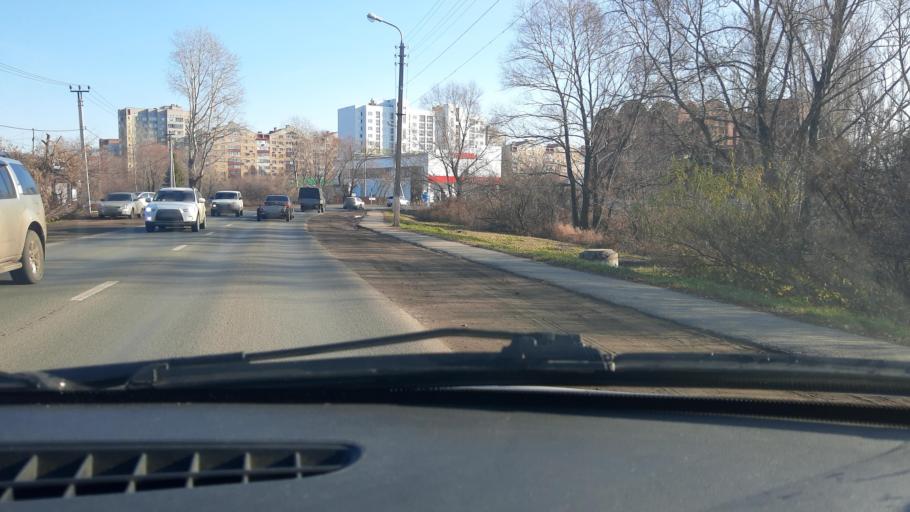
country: RU
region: Bashkortostan
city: Avdon
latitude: 54.7124
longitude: 55.8159
